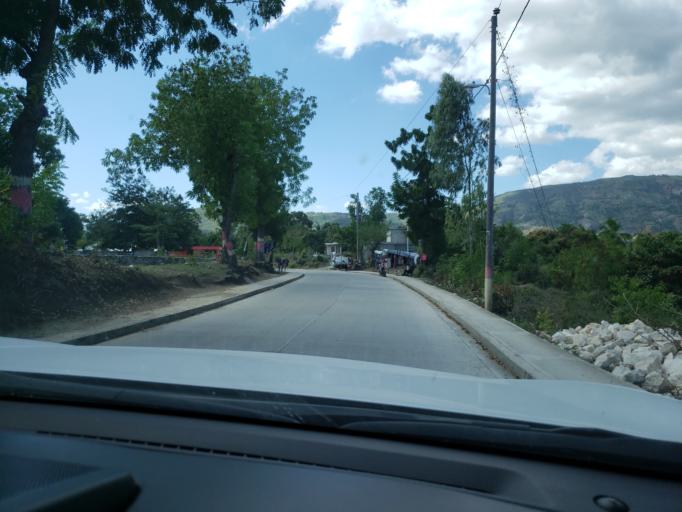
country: HT
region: Grandans
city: Anse-a-Veau
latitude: 18.4497
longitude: -73.3847
